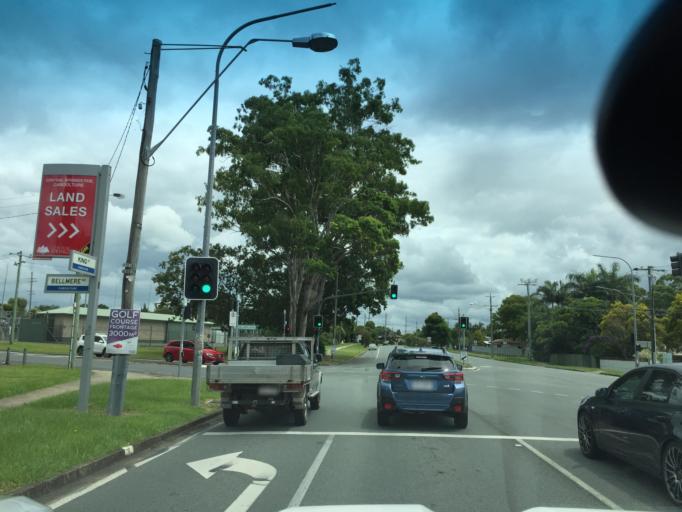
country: AU
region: Queensland
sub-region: Moreton Bay
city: Caboolture
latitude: -27.0812
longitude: 152.9355
